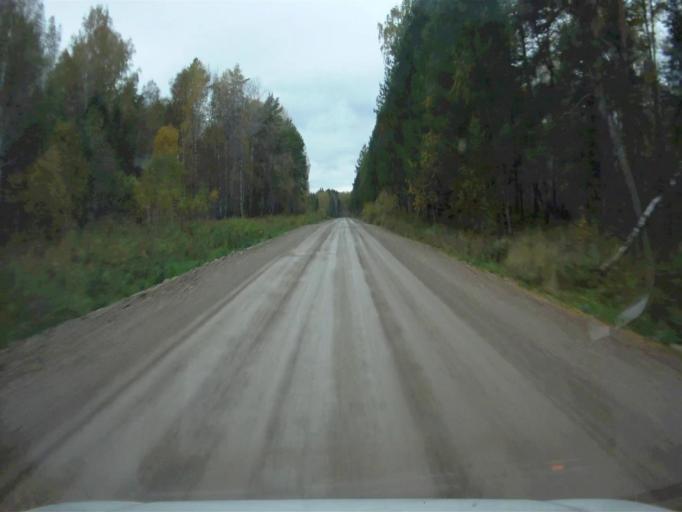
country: RU
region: Chelyabinsk
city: Nyazepetrovsk
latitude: 56.0948
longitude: 59.4033
